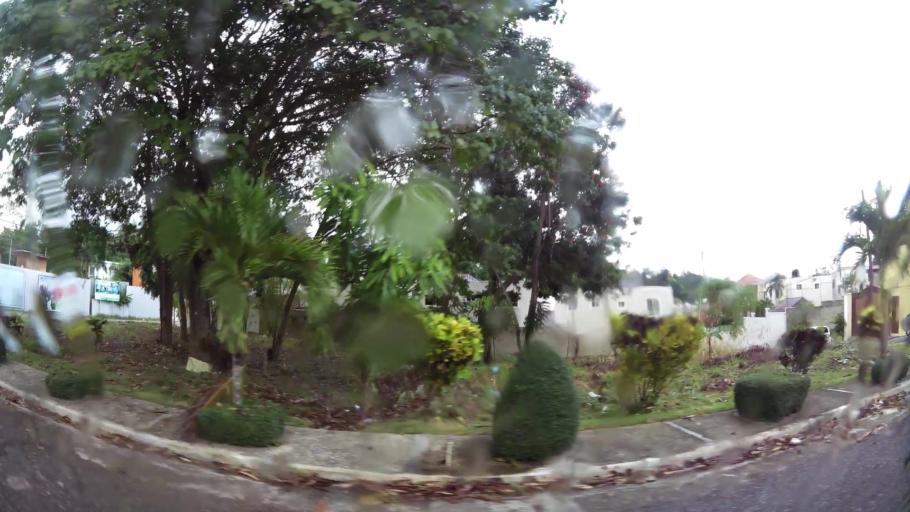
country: DO
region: Nacional
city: La Agustina
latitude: 18.5113
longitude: -69.9390
